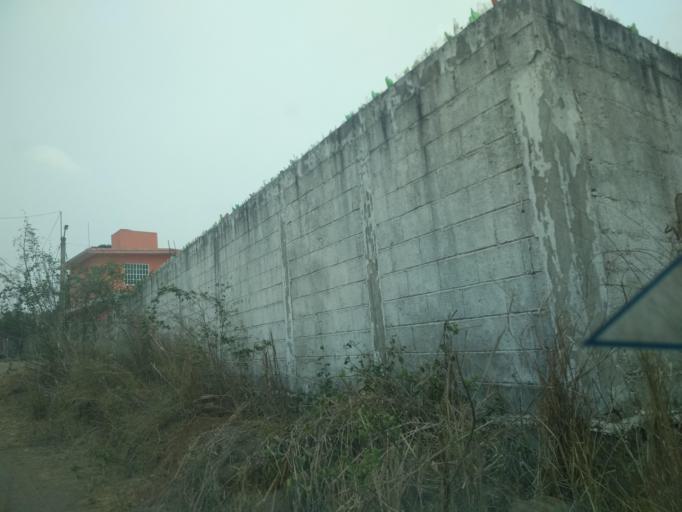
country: MX
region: Veracruz
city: Manlio Fabio Altamirano
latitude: 19.1352
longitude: -96.2961
